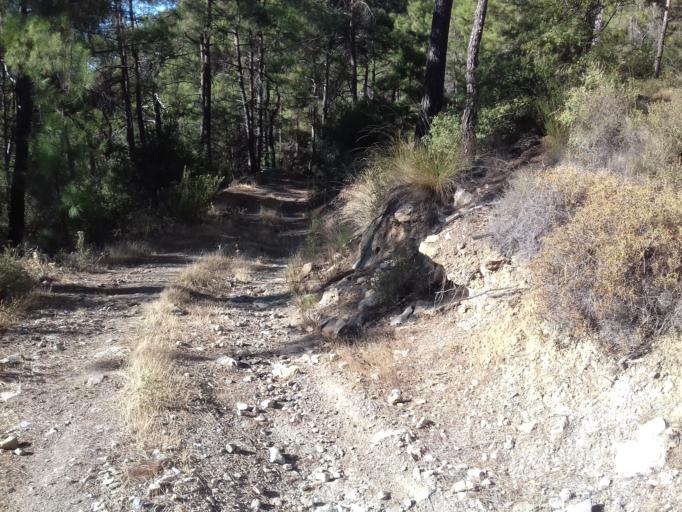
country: TR
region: Mugla
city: Yaniklar
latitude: 36.7930
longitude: 29.0240
